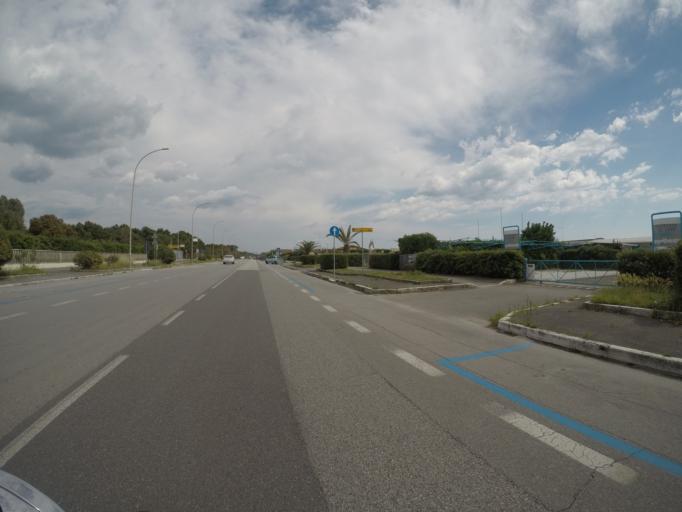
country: IT
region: Tuscany
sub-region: Provincia di Massa-Carrara
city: Massa
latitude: 44.0010
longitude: 10.1101
